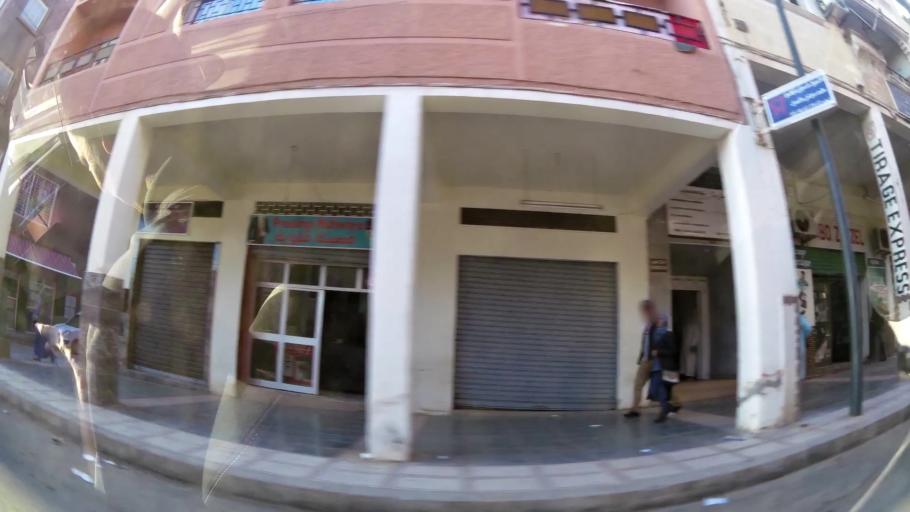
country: MA
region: Oriental
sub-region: Berkane-Taourirt
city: Berkane
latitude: 34.9209
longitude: -2.3286
